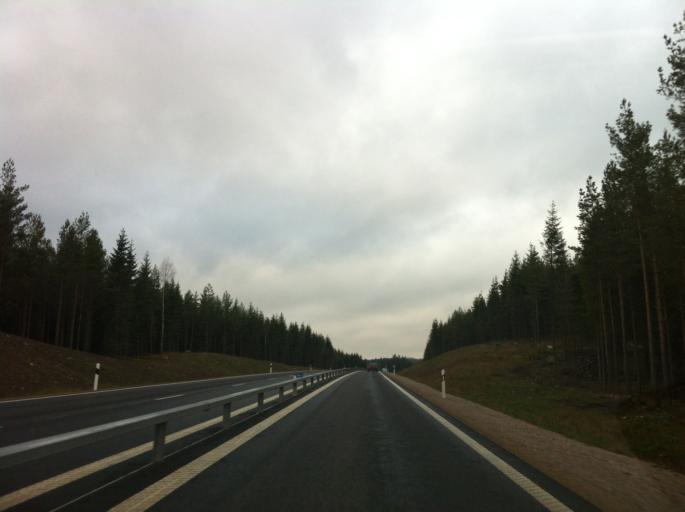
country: SE
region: Joenkoeping
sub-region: Vetlanda Kommun
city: Vetlanda
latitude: 57.4166
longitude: 15.2308
